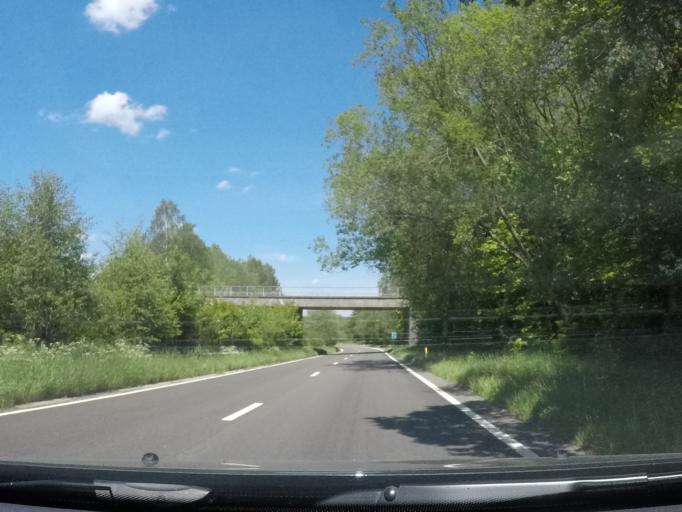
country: BE
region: Wallonia
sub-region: Province du Luxembourg
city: Saint-Hubert
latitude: 49.9878
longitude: 5.3793
